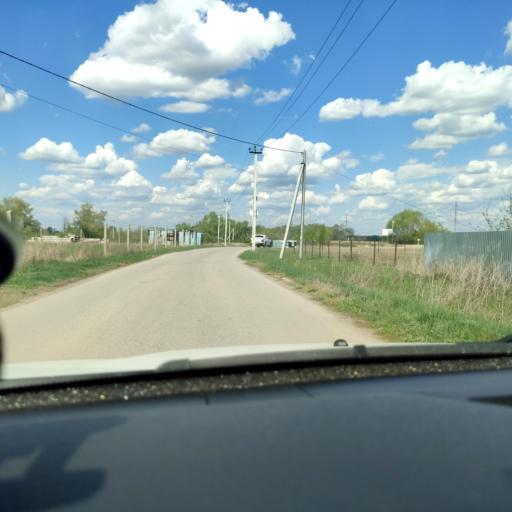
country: RU
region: Samara
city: Kinel'
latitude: 53.1661
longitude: 50.6405
